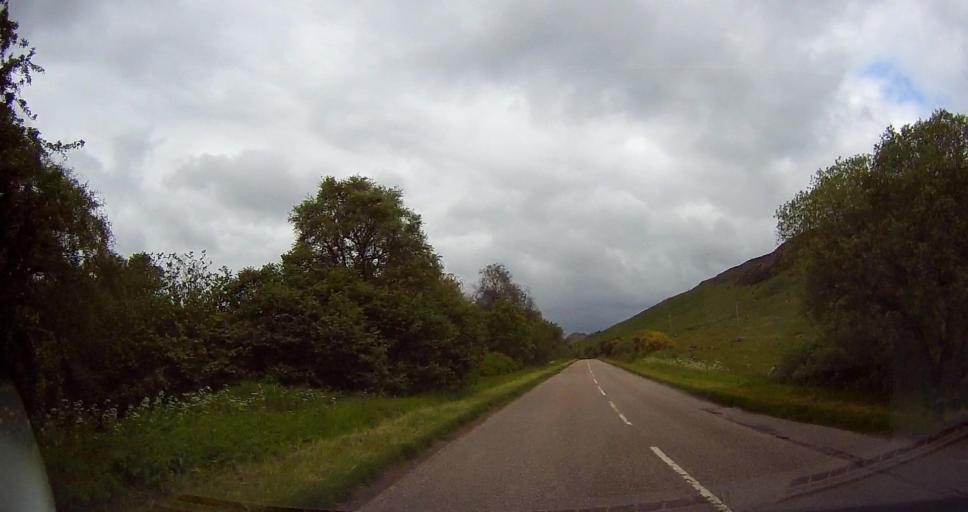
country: GB
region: Scotland
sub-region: Highland
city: Dornoch
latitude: 58.0045
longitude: -4.2194
